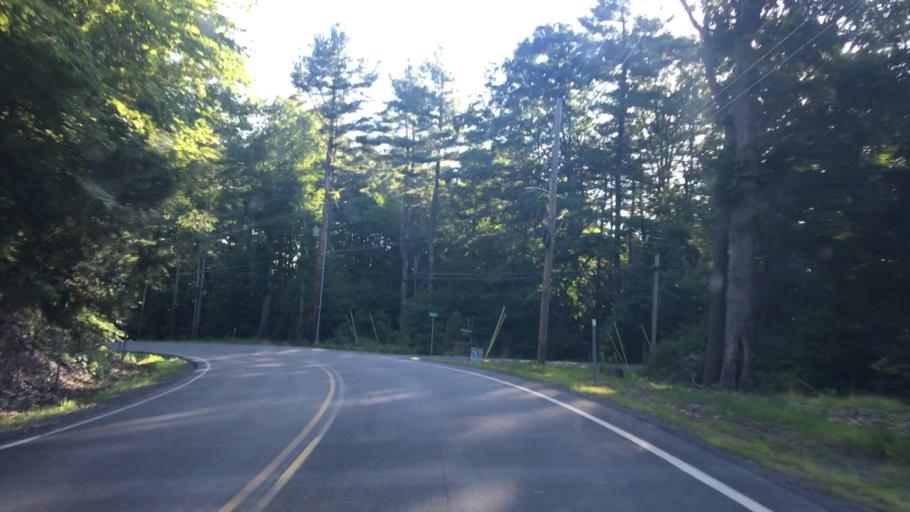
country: US
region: New Hampshire
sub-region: Rockingham County
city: Chester
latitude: 42.9565
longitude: -71.2204
